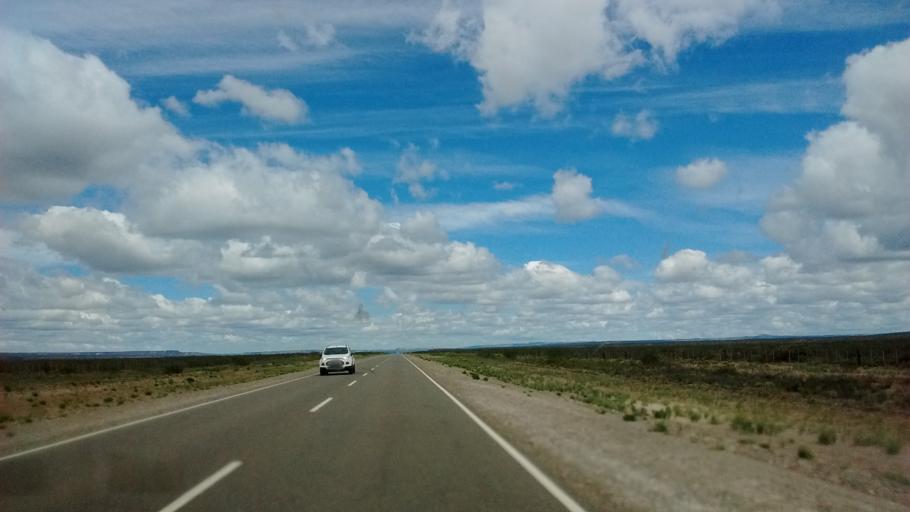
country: AR
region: Neuquen
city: Piedra del Aguila
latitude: -39.8156
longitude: -69.7251
